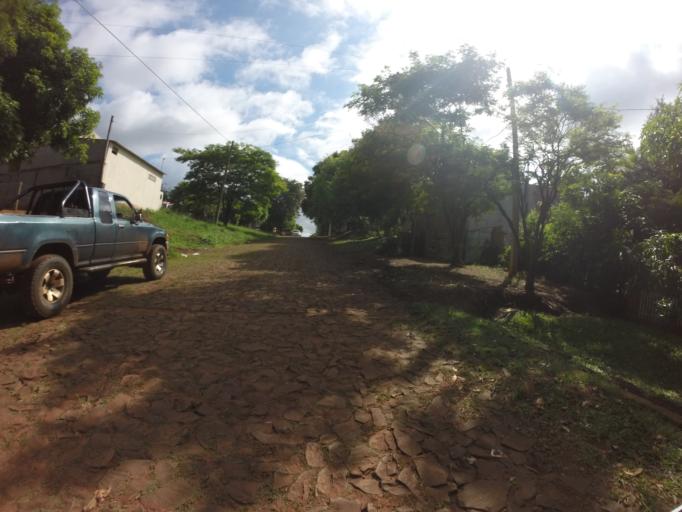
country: PY
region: Alto Parana
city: Ciudad del Este
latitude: -25.3930
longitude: -54.6444
